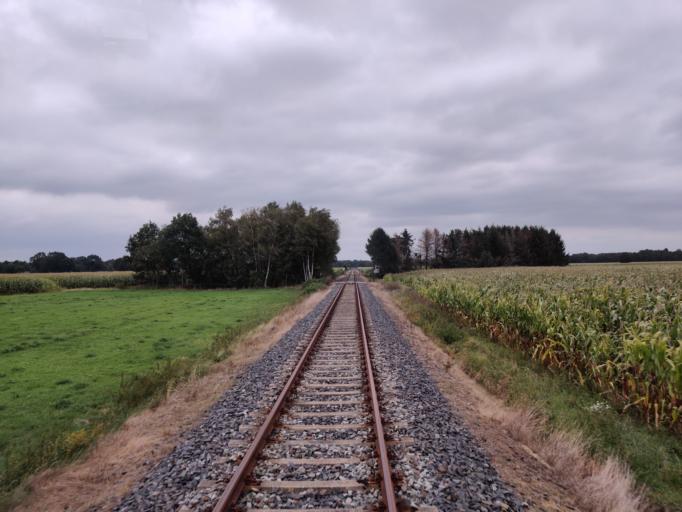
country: DE
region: Lower Saxony
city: Vollersode
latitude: 53.2820
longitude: 8.9665
